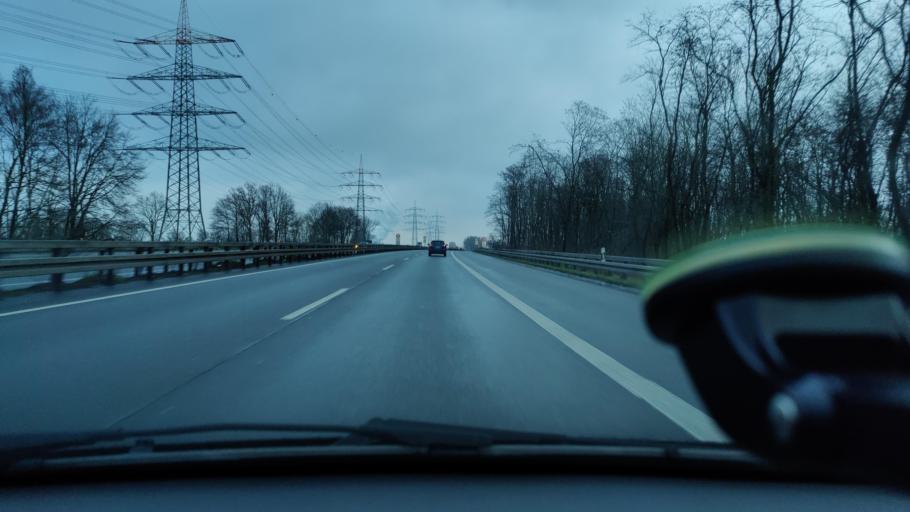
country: DE
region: North Rhine-Westphalia
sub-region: Regierungsbezirk Munster
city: Bottrop
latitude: 51.5049
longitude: 6.9384
